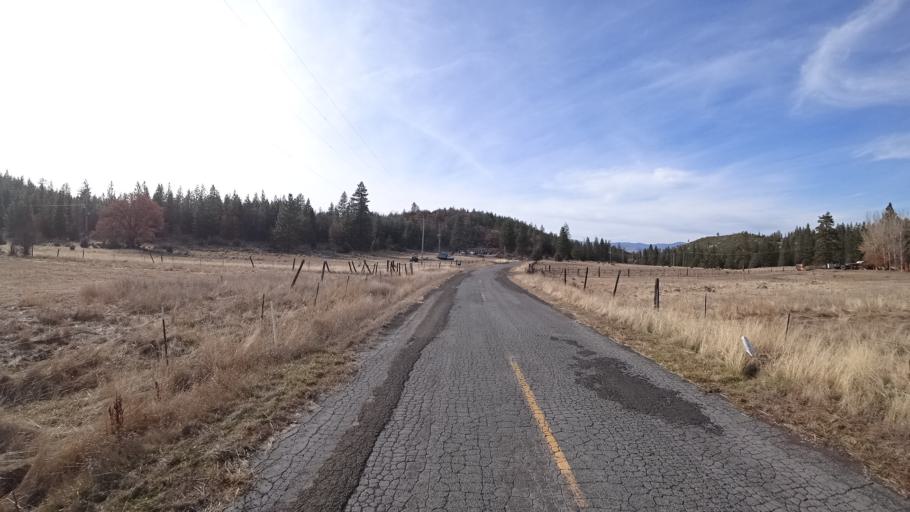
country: US
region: California
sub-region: Siskiyou County
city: Weed
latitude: 41.4650
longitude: -122.4005
